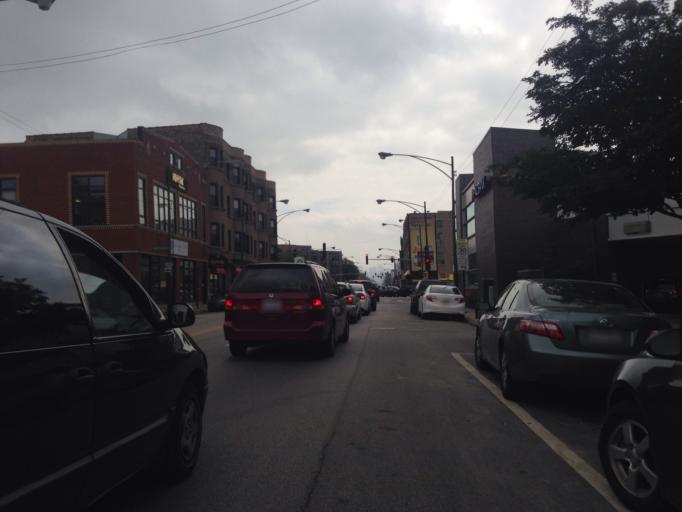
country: US
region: Illinois
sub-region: Cook County
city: Chicago
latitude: 41.9258
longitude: -87.6703
